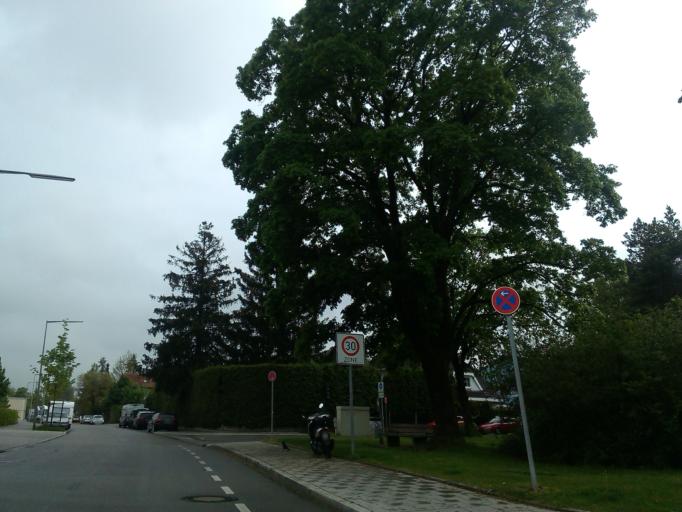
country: DE
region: Bavaria
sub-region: Upper Bavaria
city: Neubiberg
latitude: 48.1108
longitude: 11.6732
